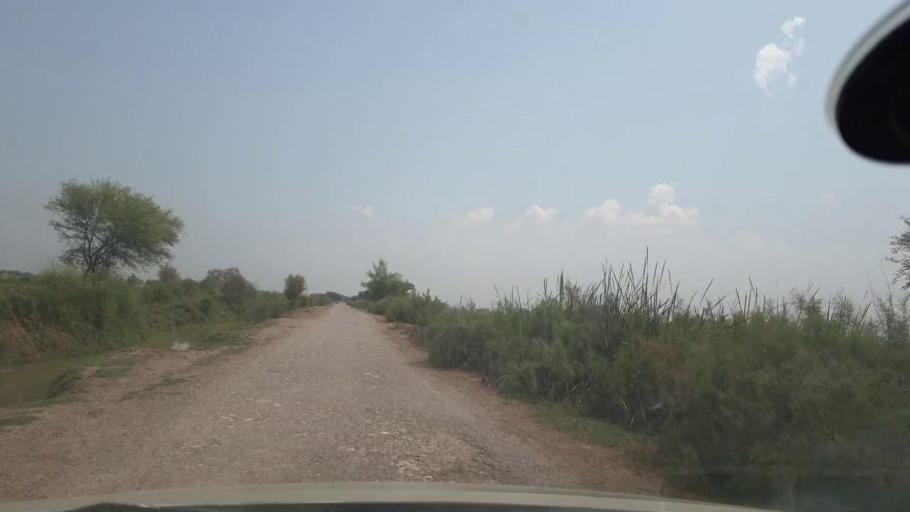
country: PK
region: Sindh
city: Jacobabad
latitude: 28.1347
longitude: 68.3776
